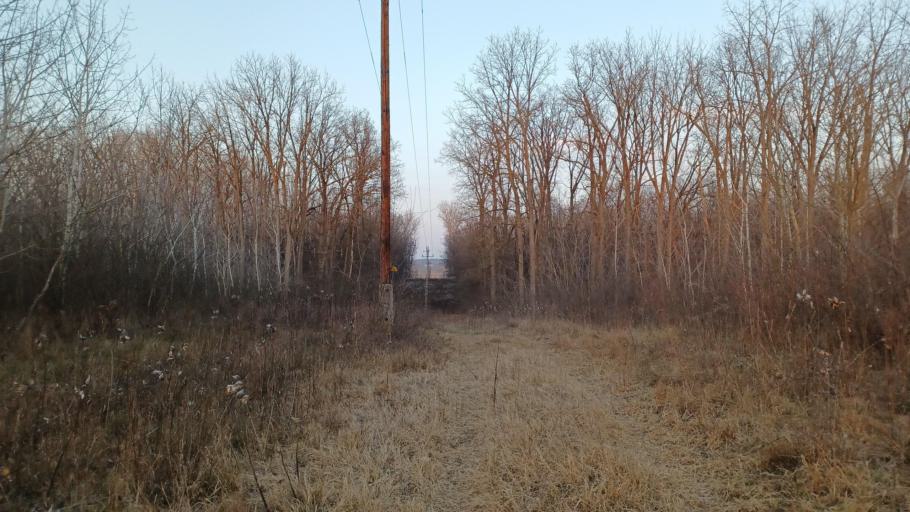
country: HU
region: Tolna
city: Tengelic
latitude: 46.5441
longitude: 18.6919
